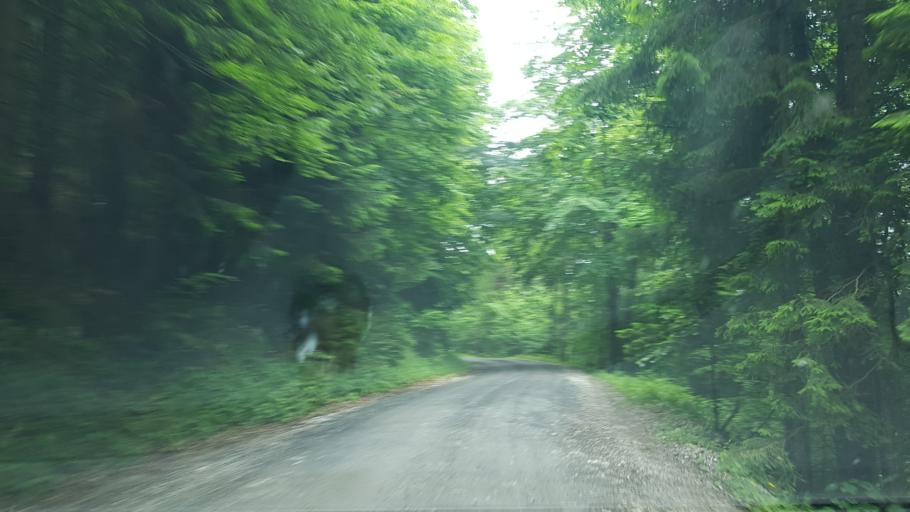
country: SI
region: Dobrna
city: Dobrna
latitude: 46.3801
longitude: 15.2406
